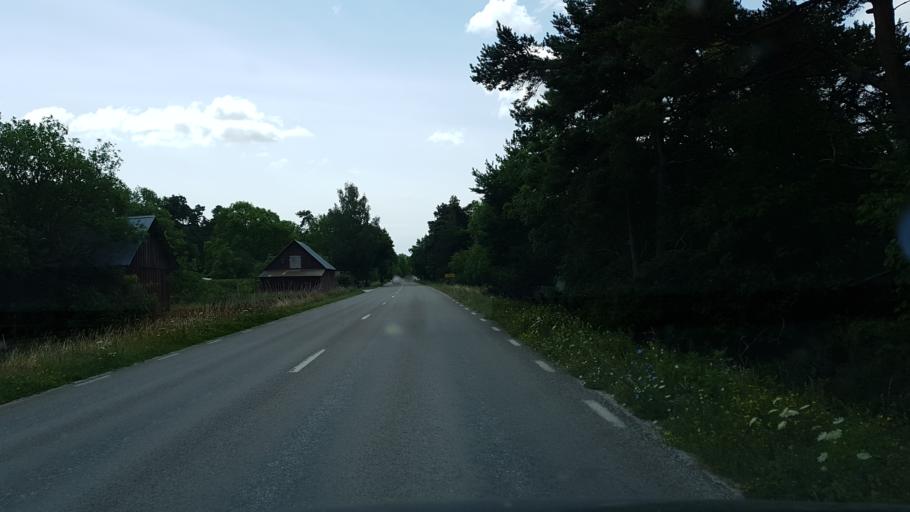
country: SE
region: Gotland
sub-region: Gotland
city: Visby
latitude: 57.7529
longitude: 18.4233
